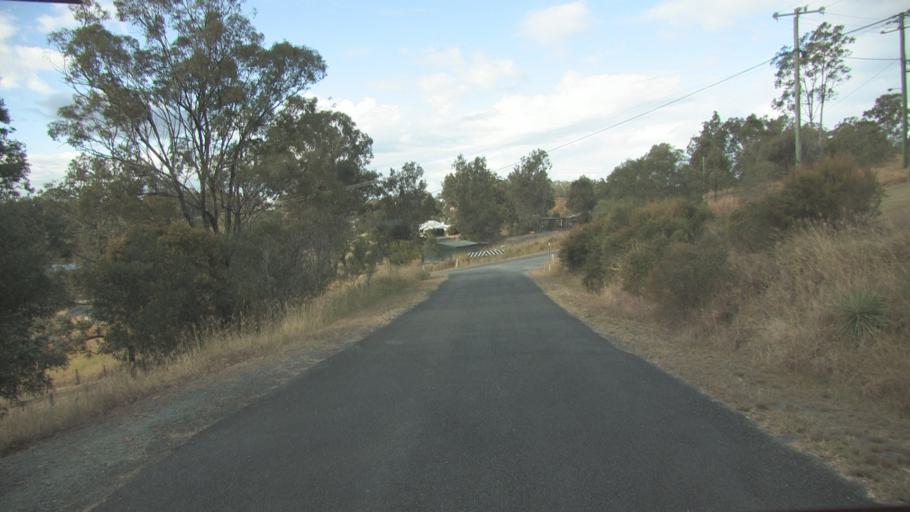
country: AU
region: Queensland
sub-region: Logan
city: Cedar Vale
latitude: -27.9035
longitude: 153.0654
